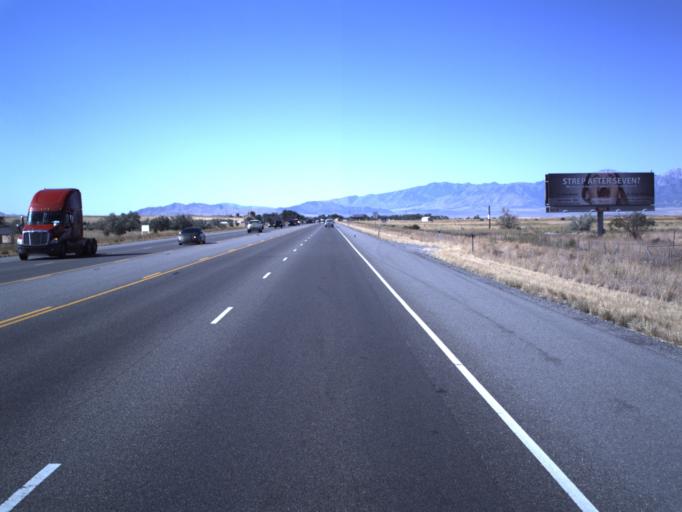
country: US
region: Utah
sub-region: Tooele County
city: Stansbury park
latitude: 40.6791
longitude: -112.2746
